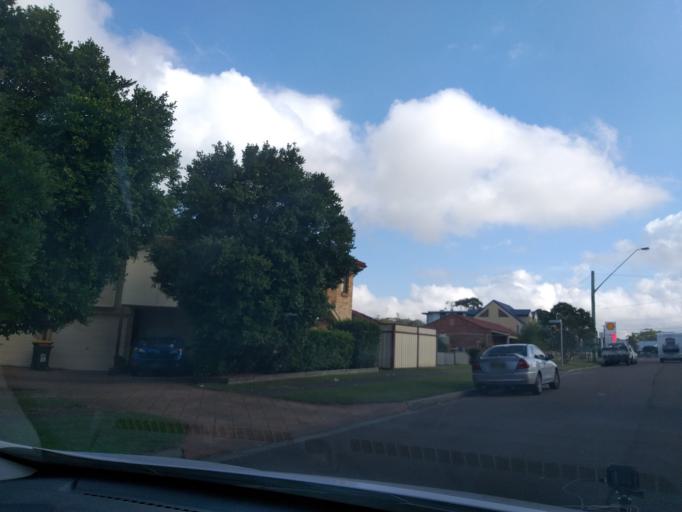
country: AU
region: New South Wales
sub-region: Wollongong
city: Helensburgh
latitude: -34.1917
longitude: 150.9785
